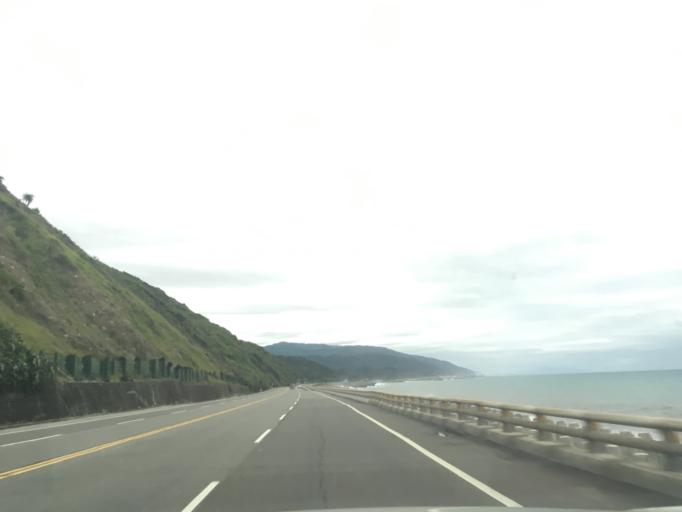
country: TW
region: Taiwan
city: Hengchun
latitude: 22.3153
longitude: 120.8914
